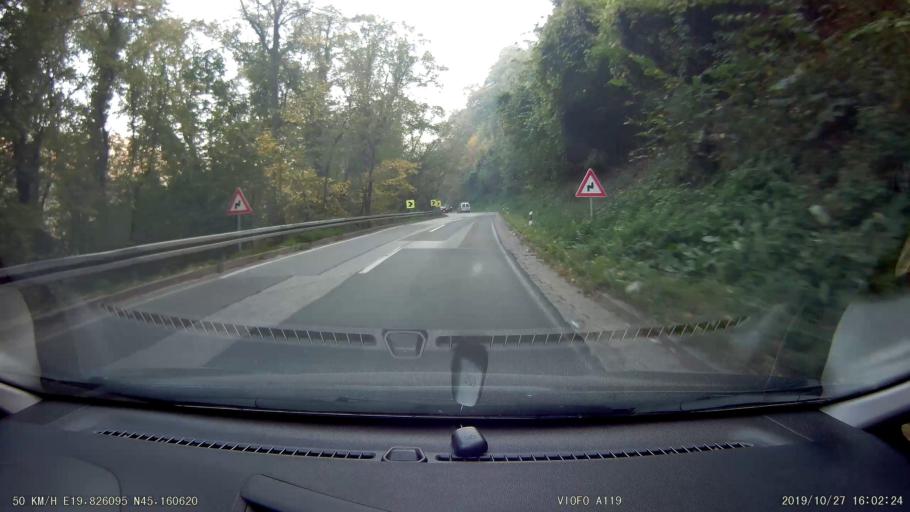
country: RS
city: Vrdnik
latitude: 45.1605
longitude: 19.8262
